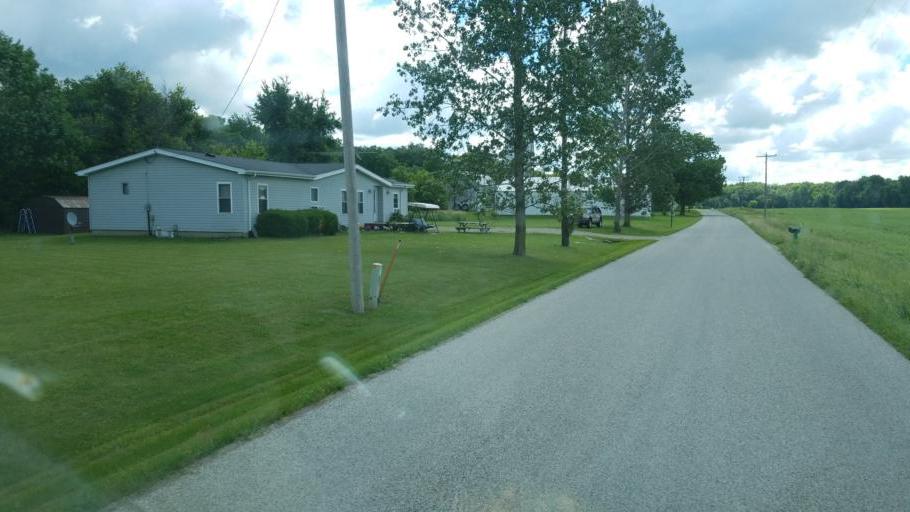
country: US
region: Ohio
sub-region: Morrow County
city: Mount Gilead
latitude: 40.5440
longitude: -82.8528
